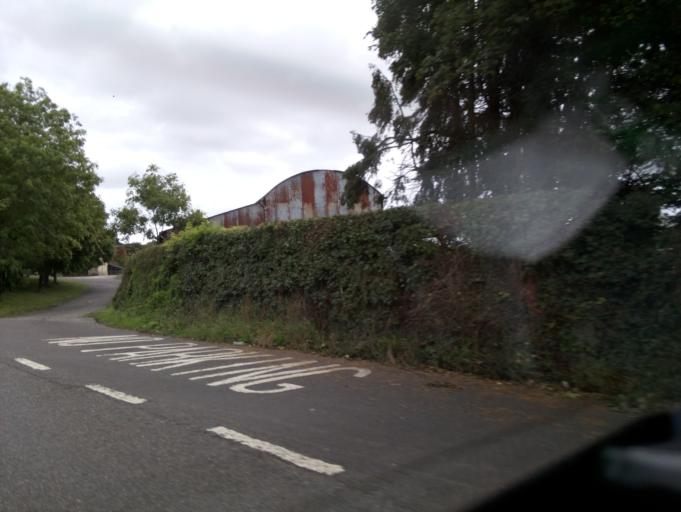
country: GB
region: England
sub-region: Devon
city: Kingsteignton
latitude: 50.5459
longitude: -3.5779
